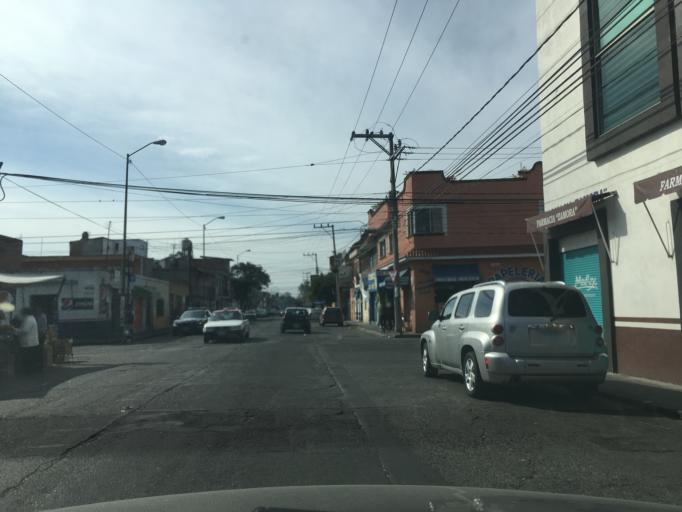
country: MX
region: Michoacan
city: Morelia
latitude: 19.6956
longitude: -101.1974
